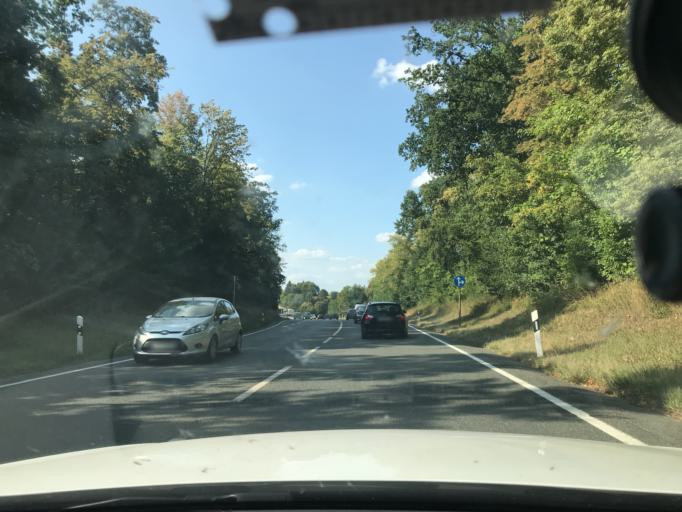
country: DE
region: Bavaria
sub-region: Upper Palatinate
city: Sulzbach-Rosenberg
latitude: 49.4944
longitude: 11.7318
